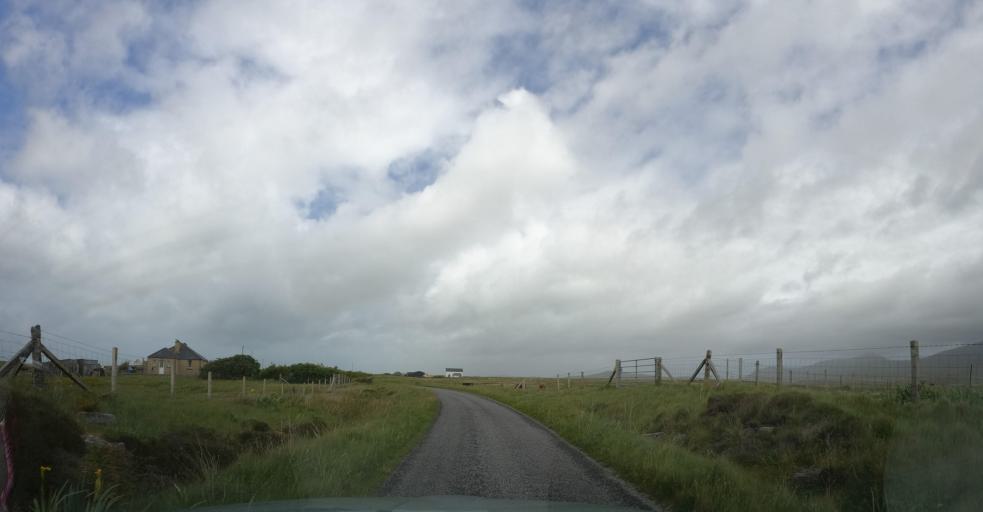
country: GB
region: Scotland
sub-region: Eilean Siar
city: Isle of South Uist
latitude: 57.2556
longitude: -7.4044
